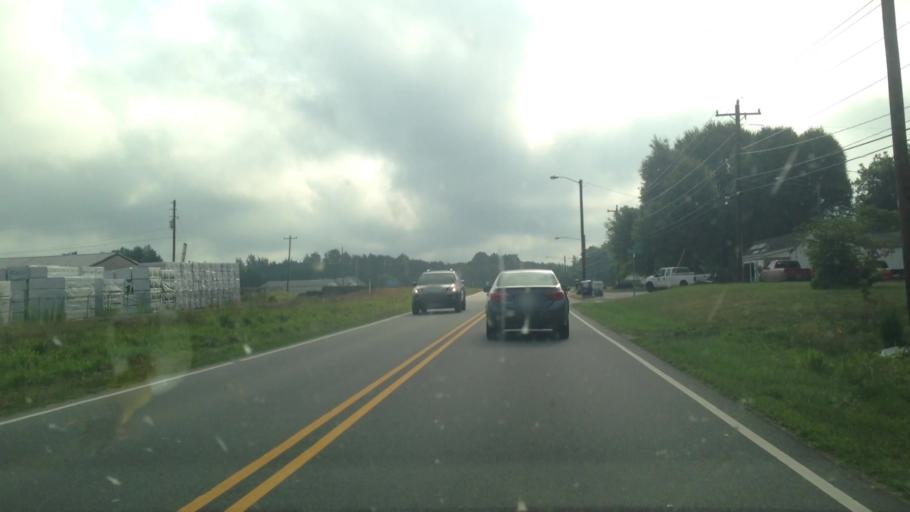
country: US
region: North Carolina
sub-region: Forsyth County
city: Kernersville
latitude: 36.1359
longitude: -80.1118
